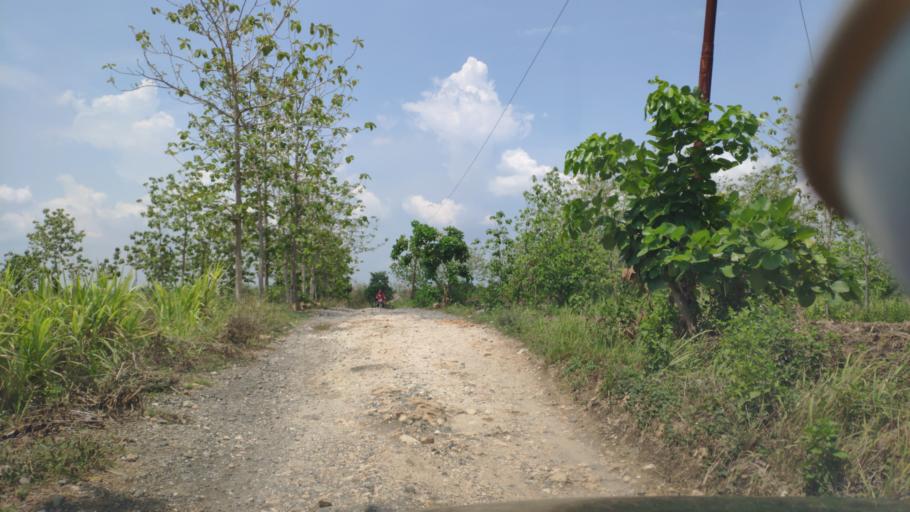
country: ID
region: Central Java
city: Balong Wetan
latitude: -7.0064
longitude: 111.2537
